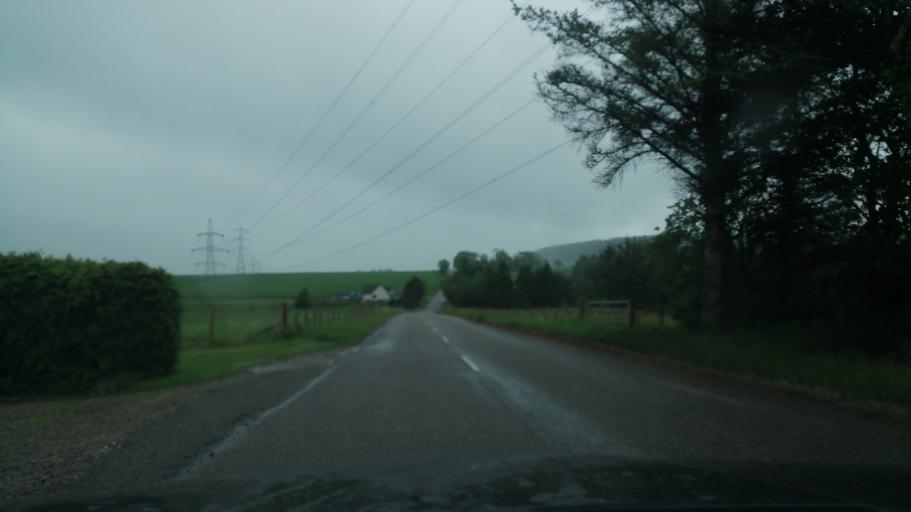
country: GB
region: Scotland
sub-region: Aberdeenshire
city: Huntly
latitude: 57.5442
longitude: -2.8049
